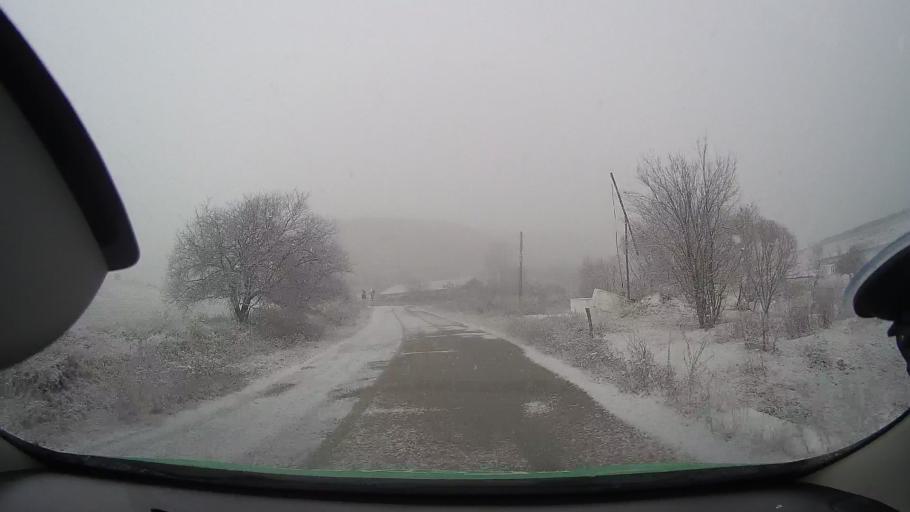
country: RO
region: Alba
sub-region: Comuna Hoparta
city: Hoparta
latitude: 46.3122
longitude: 23.8599
